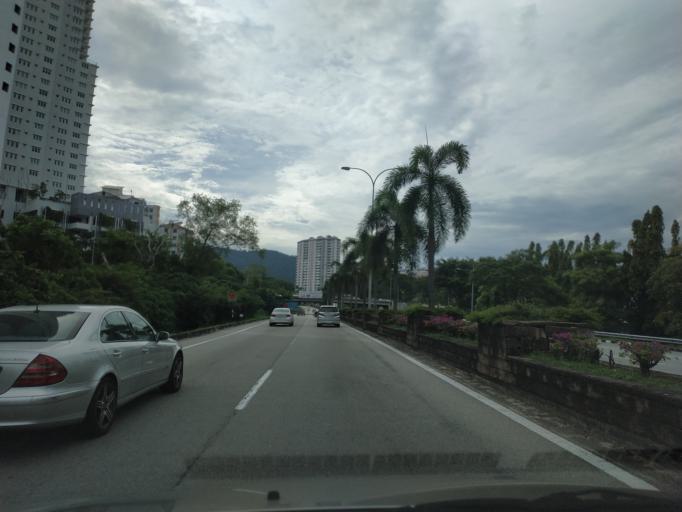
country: MY
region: Penang
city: George Town
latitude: 5.3793
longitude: 100.3151
